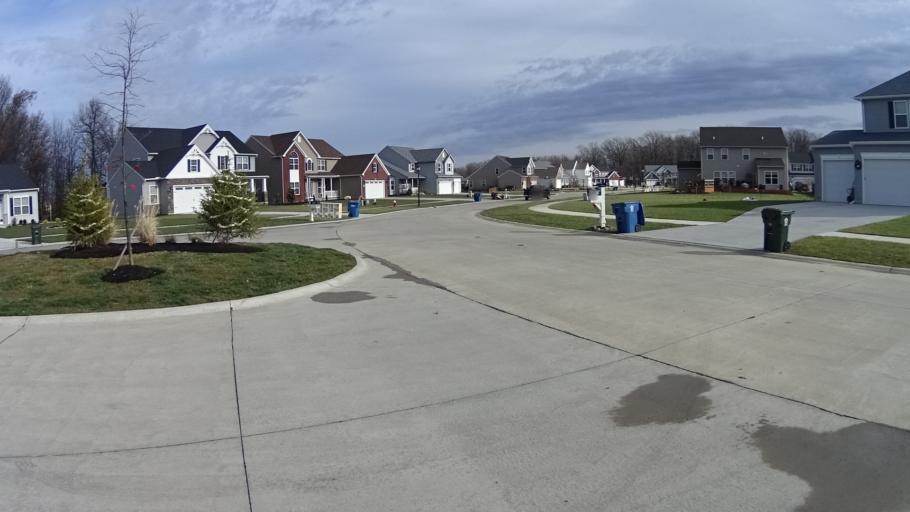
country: US
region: Ohio
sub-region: Lorain County
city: North Ridgeville
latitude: 41.3621
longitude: -82.0489
